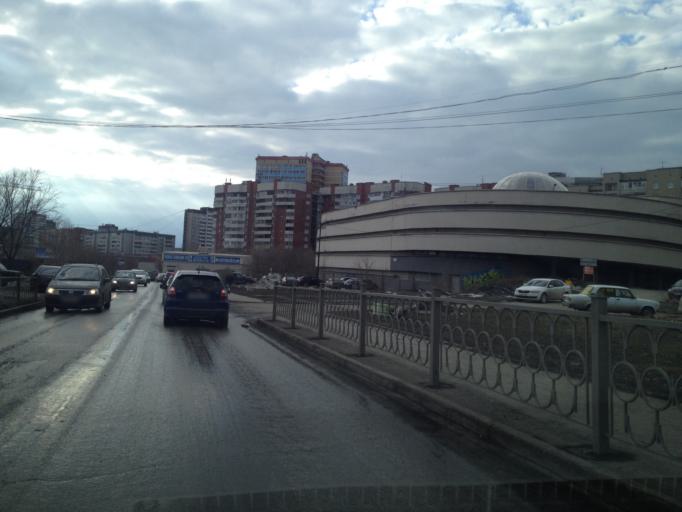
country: RU
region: Sverdlovsk
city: Yekaterinburg
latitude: 56.8528
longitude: 60.5789
